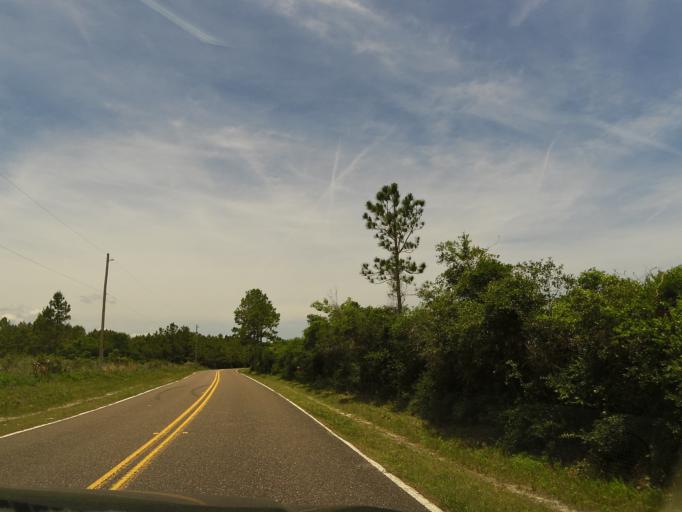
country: US
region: Florida
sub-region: Duval County
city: Atlantic Beach
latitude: 30.4779
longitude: -81.4868
